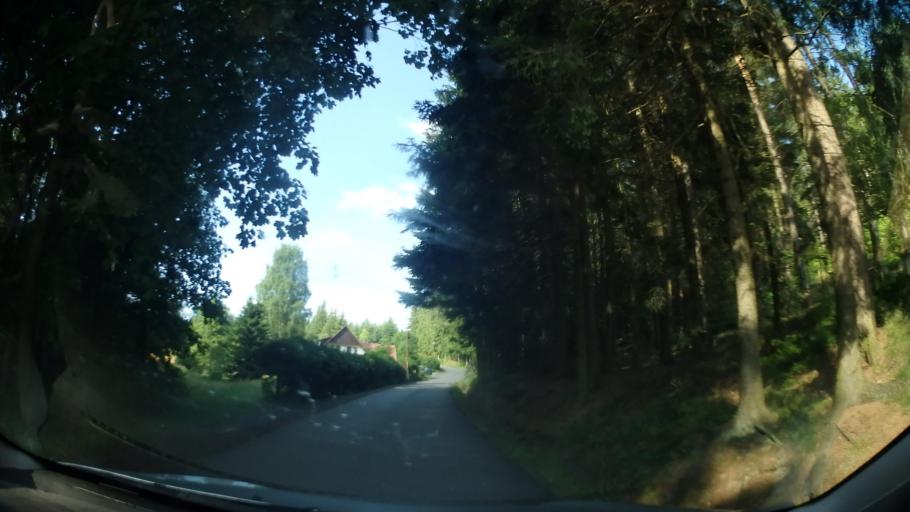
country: CZ
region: Vysocina
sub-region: Okres Zd'ar nad Sazavou
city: Svratka
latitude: 49.7249
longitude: 16.0422
